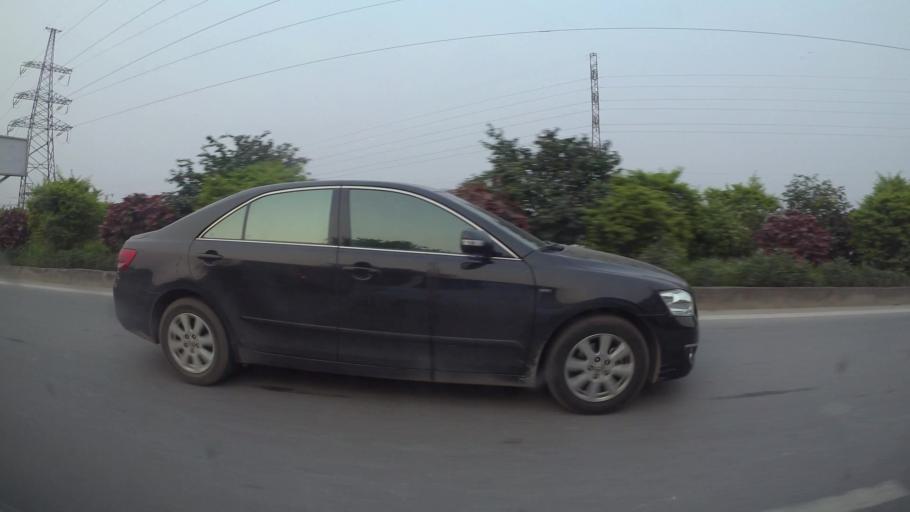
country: VN
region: Ha Noi
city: Ha Dong
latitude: 20.9954
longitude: 105.7352
